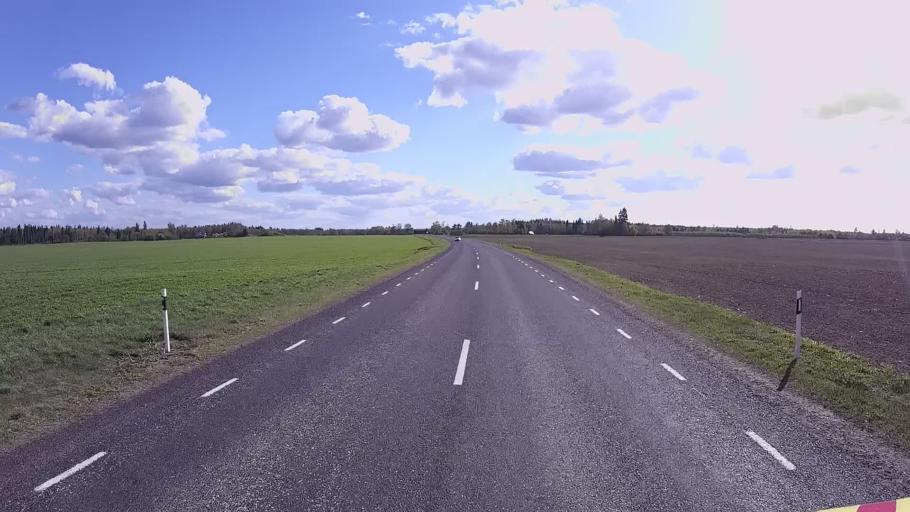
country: EE
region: Jogevamaa
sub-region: Jogeva linn
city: Jogeva
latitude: 58.7252
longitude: 26.1921
